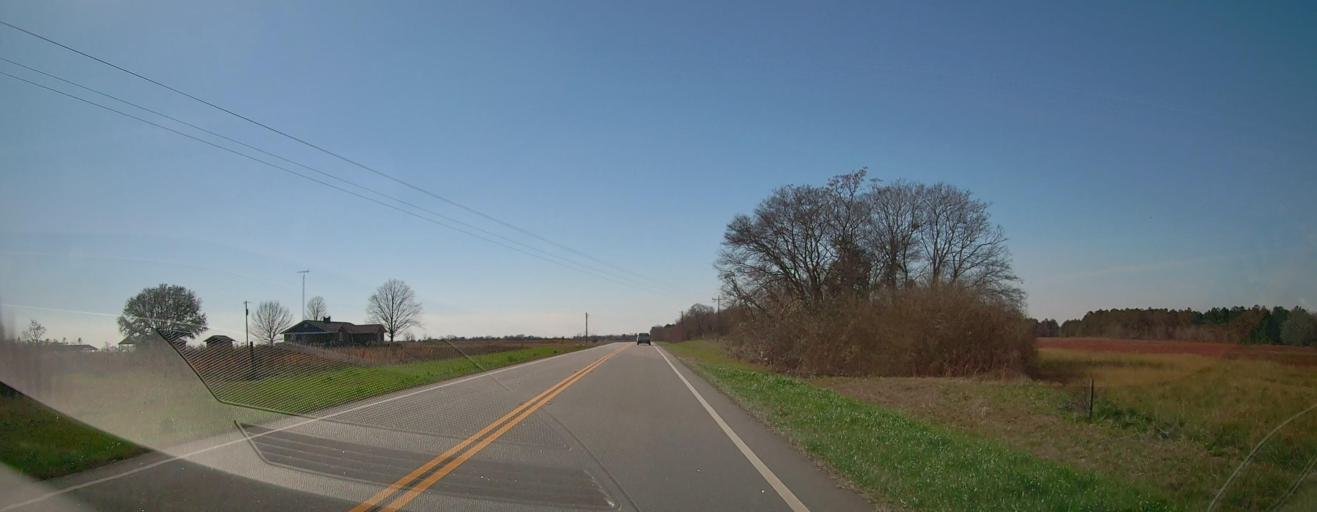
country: US
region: Georgia
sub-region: Dooly County
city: Unadilla
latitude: 32.3377
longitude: -83.8196
